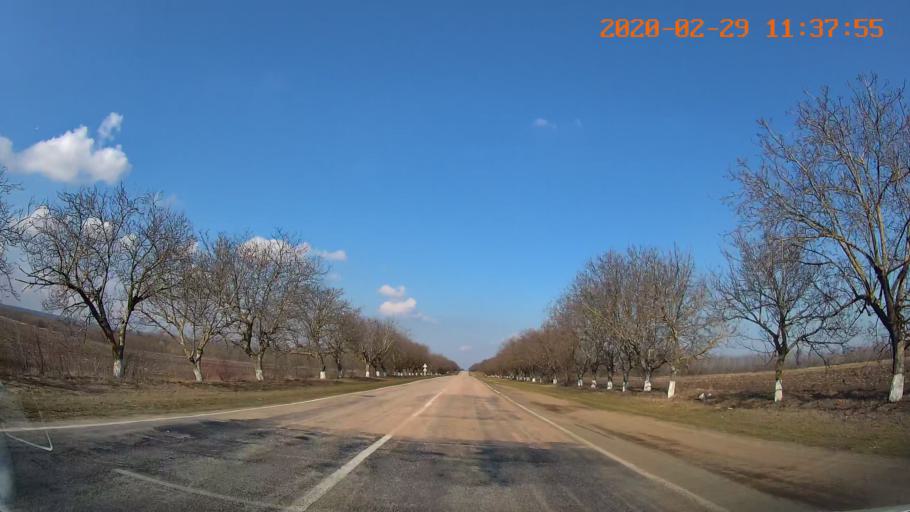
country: MD
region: Rezina
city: Saharna
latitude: 47.6182
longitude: 29.0415
